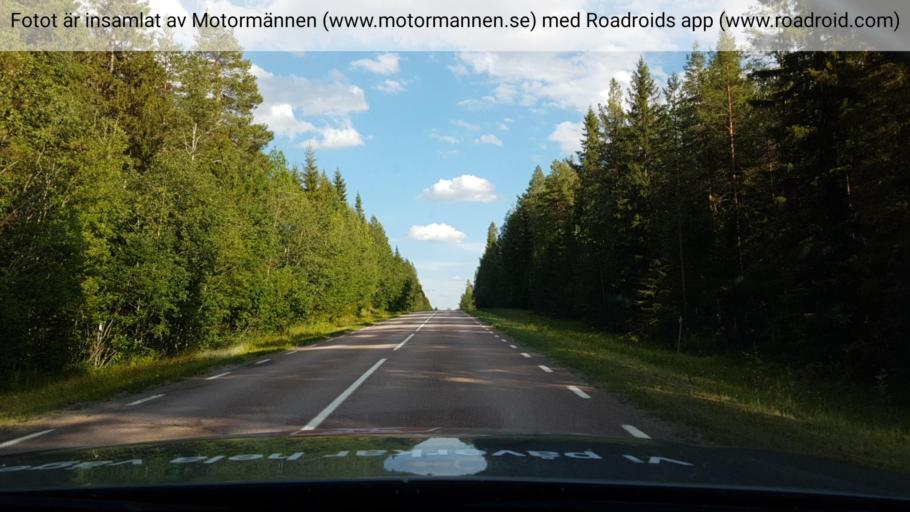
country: SE
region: Jaemtland
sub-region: Stroemsunds Kommun
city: Stroemsund
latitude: 63.6833
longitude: 15.9164
